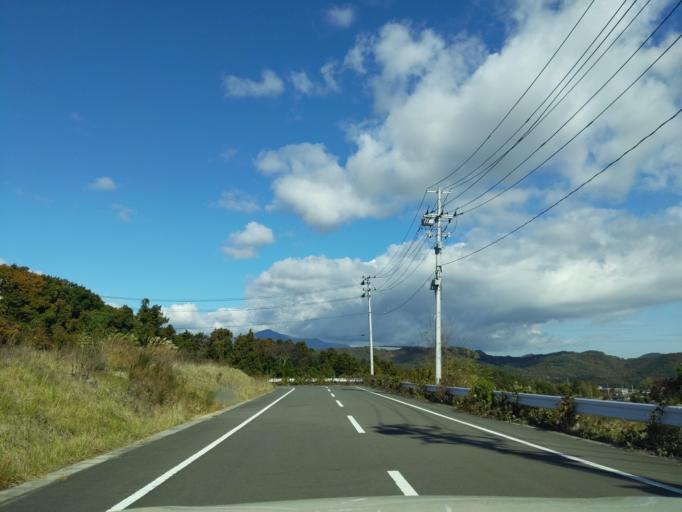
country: JP
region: Fukushima
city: Koriyama
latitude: 37.4643
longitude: 140.3035
